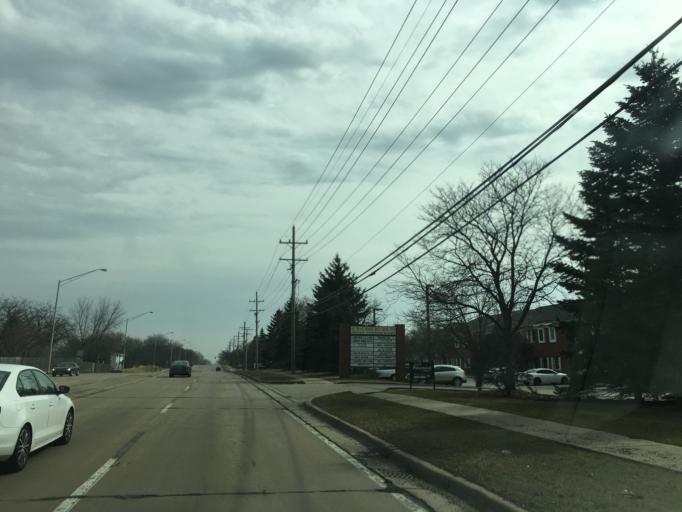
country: US
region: Illinois
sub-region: DuPage County
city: Roselle
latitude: 42.0042
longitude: -88.1075
